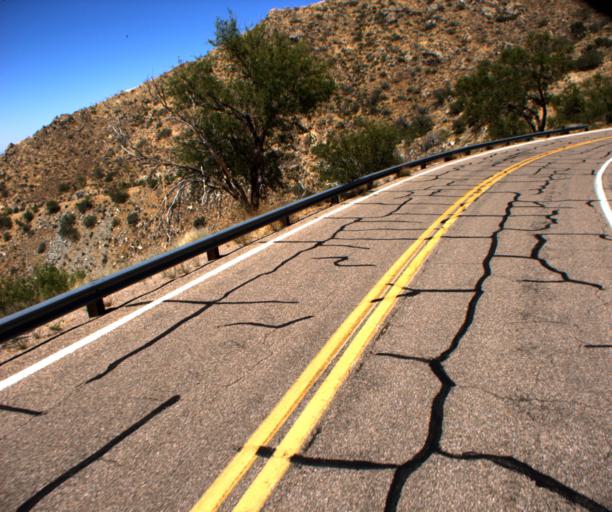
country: US
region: Arizona
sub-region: Pima County
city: Sells
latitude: 31.9809
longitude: -111.6027
